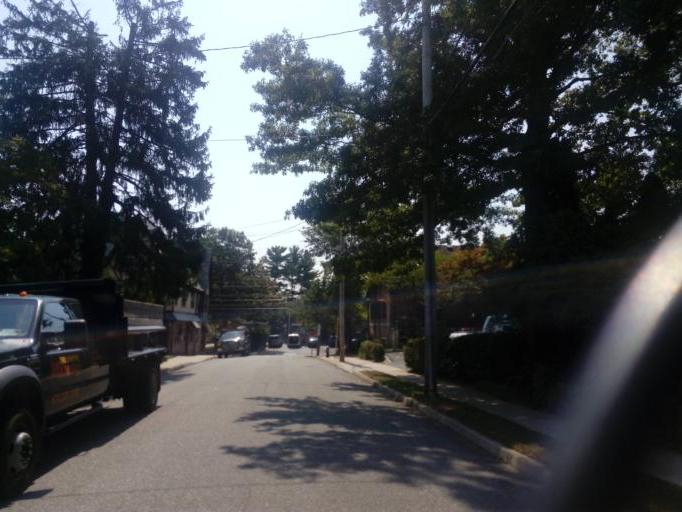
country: US
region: New York
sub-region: Nassau County
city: Locust Valley
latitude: 40.8763
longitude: -73.5994
